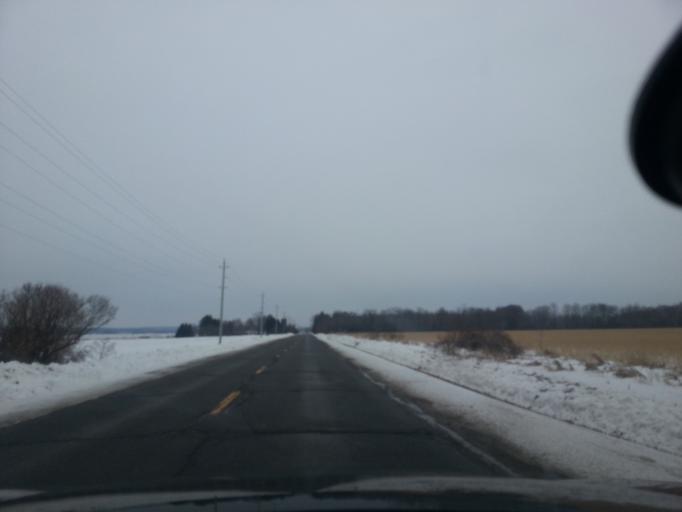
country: CA
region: Ontario
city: Arnprior
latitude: 45.3774
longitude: -76.2120
